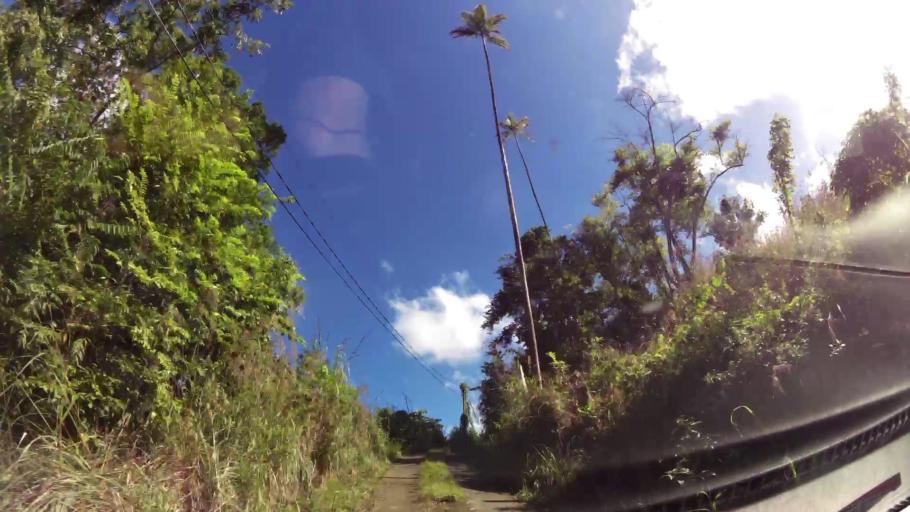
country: DM
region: Saint John
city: Portsmouth
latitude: 15.5532
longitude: -61.4552
